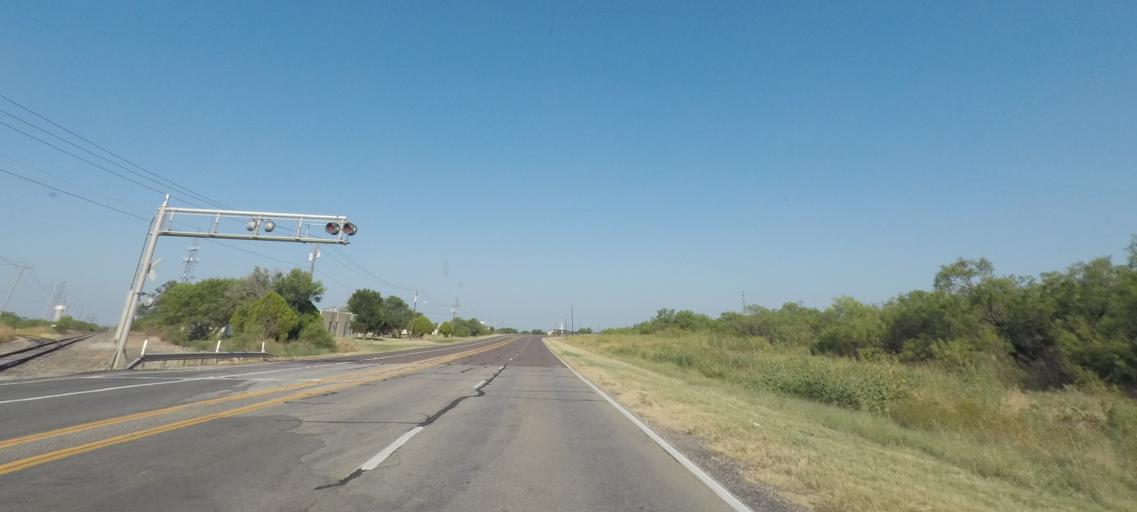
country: US
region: Texas
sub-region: Archer County
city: Holliday
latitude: 33.8595
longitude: -98.5919
